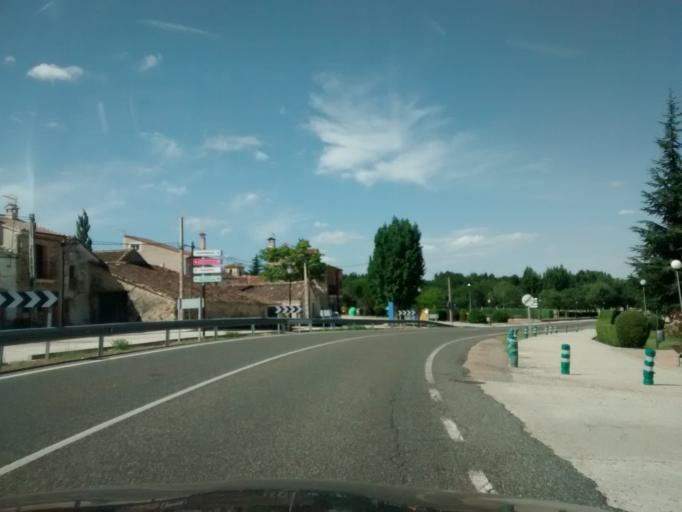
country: ES
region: Castille and Leon
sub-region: Provincia de Segovia
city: Collado Hermoso
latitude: 41.0384
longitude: -3.9182
